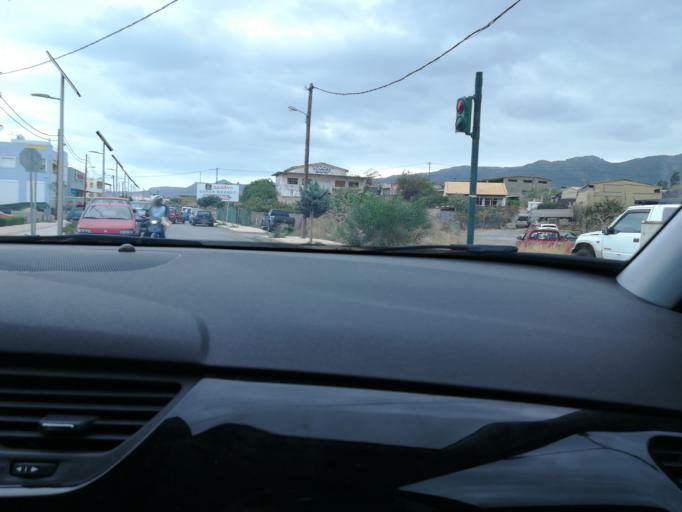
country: GR
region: Crete
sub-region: Nomos Lasithiou
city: Siteia
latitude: 35.2042
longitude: 26.1049
